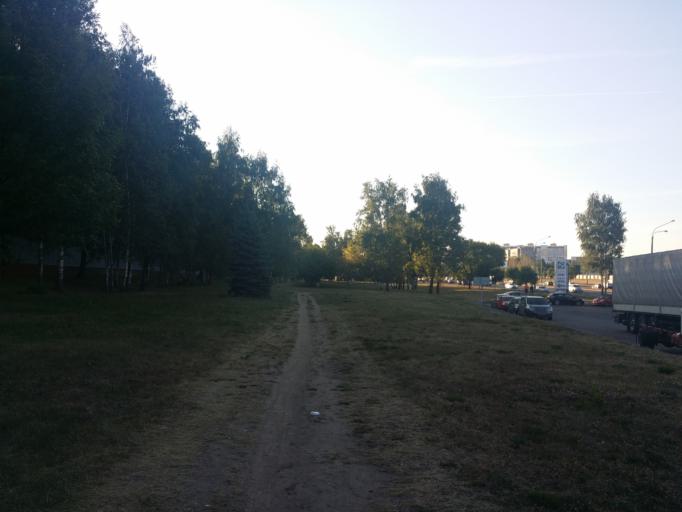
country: BY
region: Minsk
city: Vyaliki Trastsyanets
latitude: 53.8529
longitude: 27.6940
